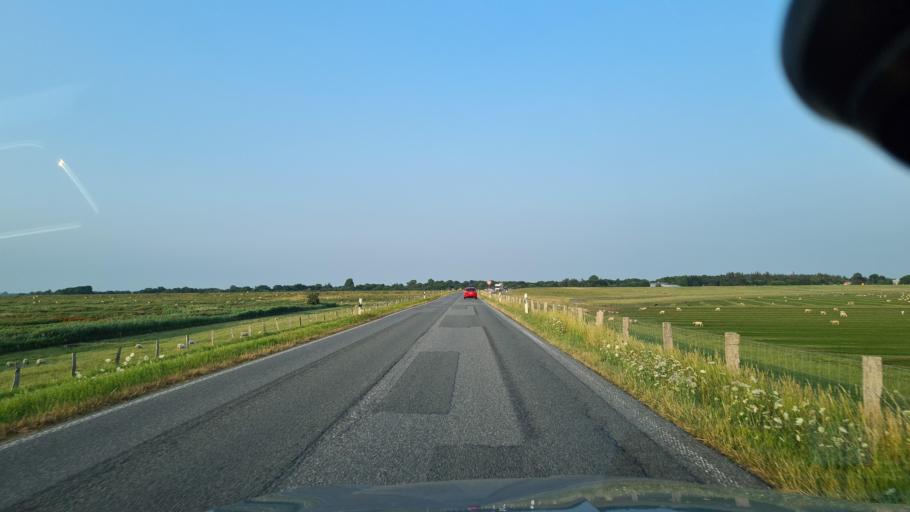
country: DE
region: Schleswig-Holstein
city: Wobbenbull
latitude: 54.5238
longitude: 8.9793
